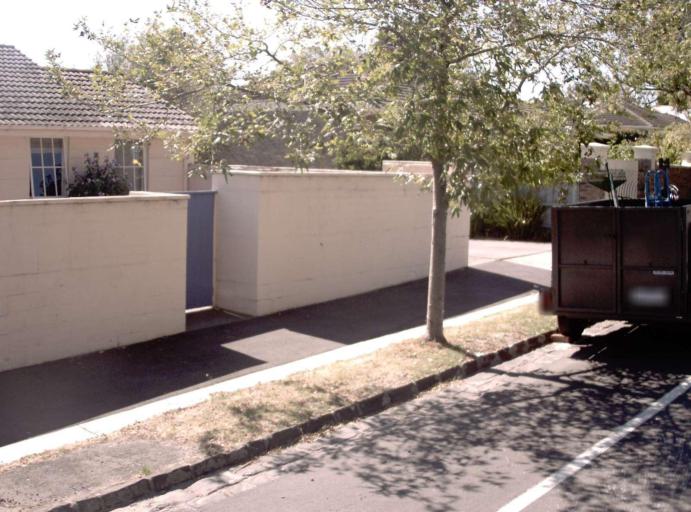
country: AU
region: Victoria
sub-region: Bayside
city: Hampton
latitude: -37.9245
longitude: 145.0050
